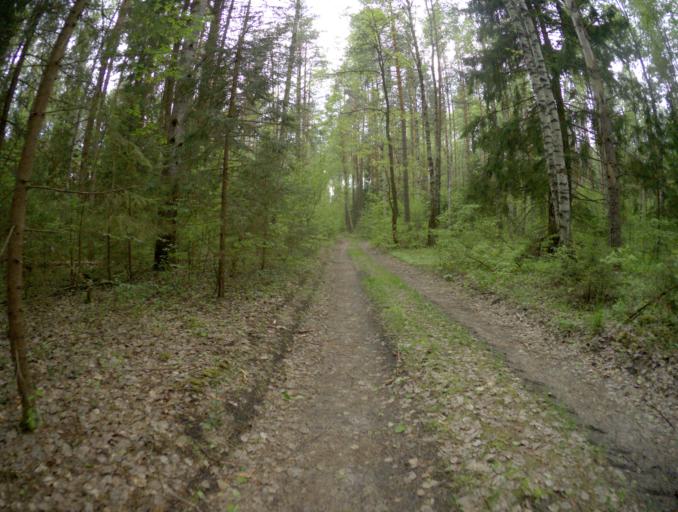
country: RU
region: Rjazan
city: Gus'-Zheleznyy
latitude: 55.1273
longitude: 41.1513
